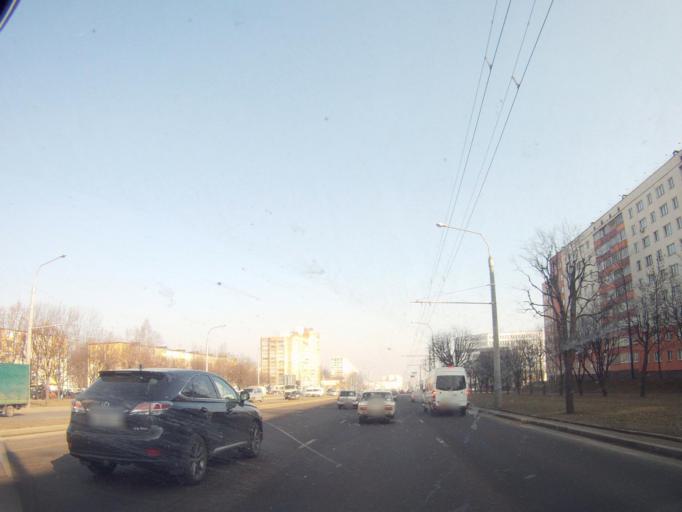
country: BY
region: Minsk
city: Novoye Medvezhino
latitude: 53.9182
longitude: 27.4962
